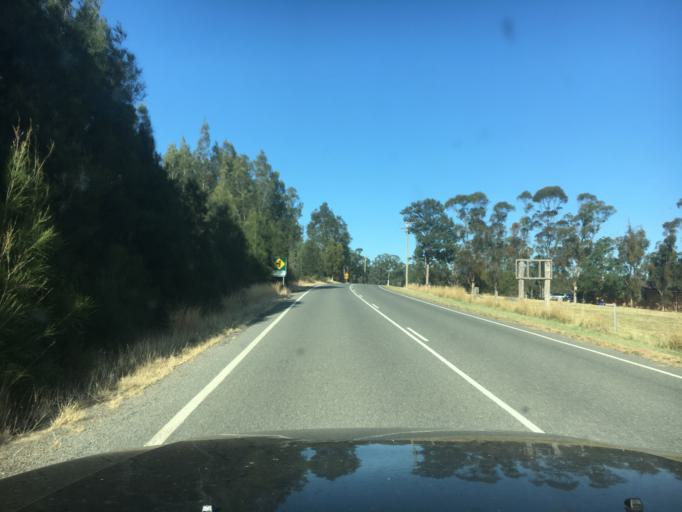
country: AU
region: New South Wales
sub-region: Singleton
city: Singleton
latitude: -32.5468
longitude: 151.2402
